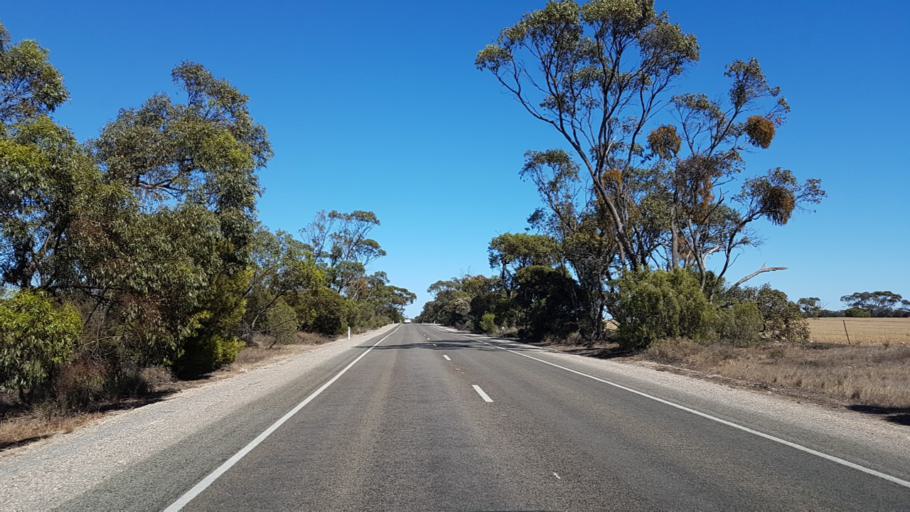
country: AU
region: South Australia
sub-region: Copper Coast
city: Kadina
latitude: -34.0469
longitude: 137.9570
